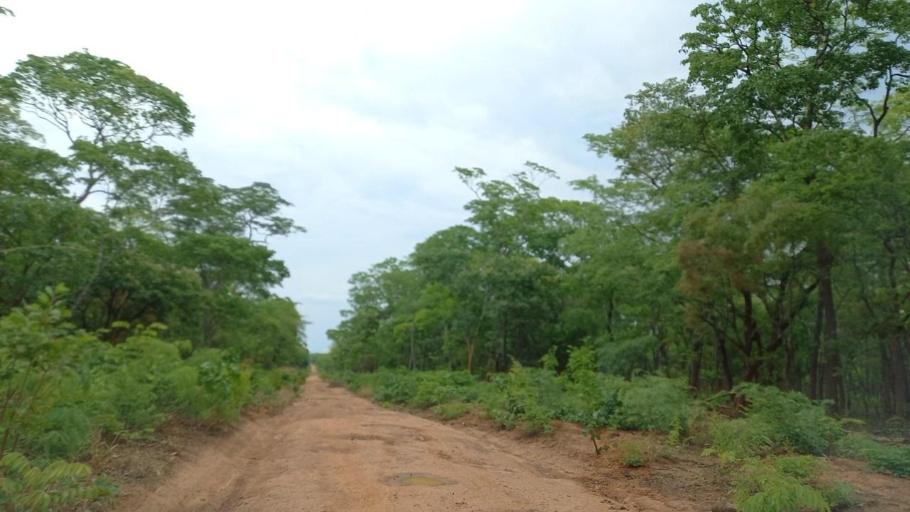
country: ZM
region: North-Western
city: Kalengwa
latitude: -13.5824
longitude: 24.9715
